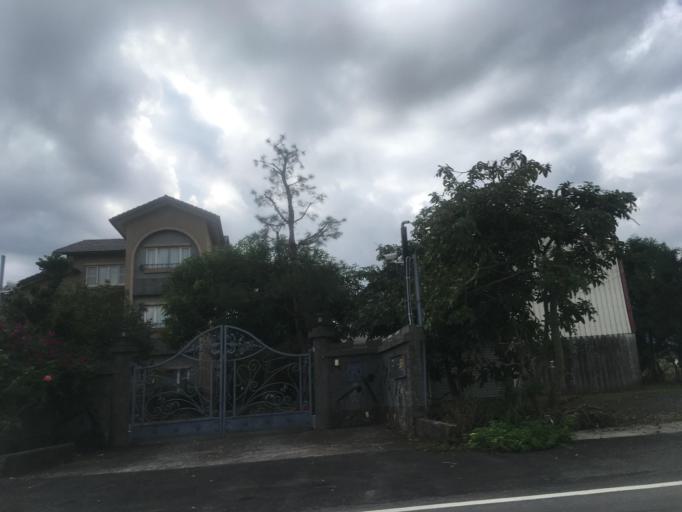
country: TW
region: Taiwan
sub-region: Yilan
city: Yilan
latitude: 24.6857
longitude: 121.7099
